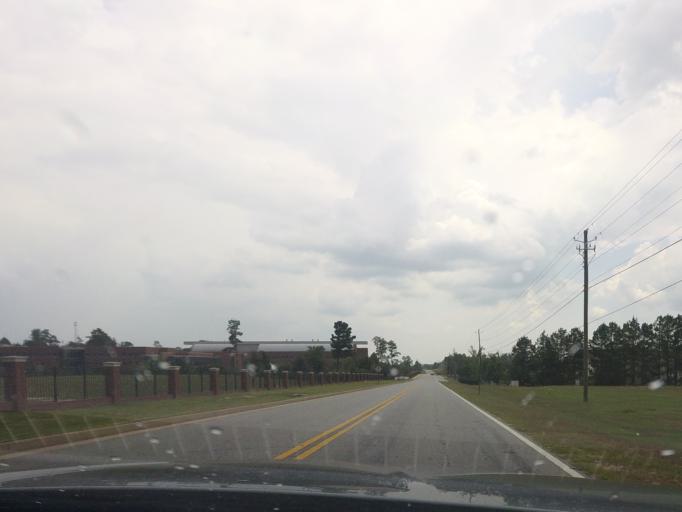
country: US
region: Georgia
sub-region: Bibb County
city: West Point
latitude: 32.8119
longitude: -83.7362
